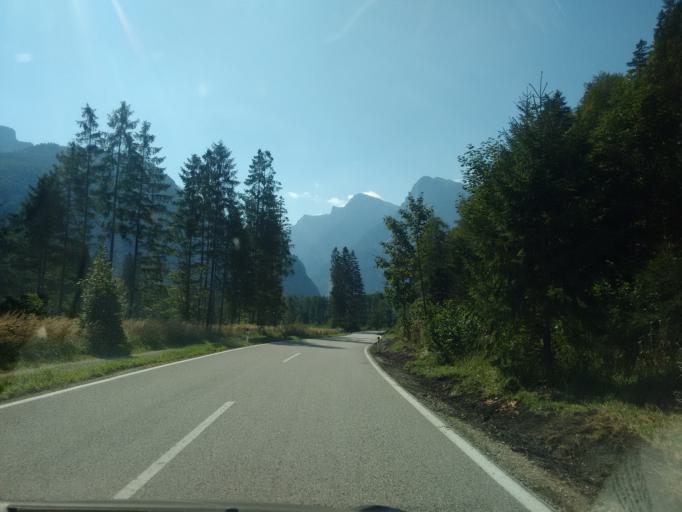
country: AT
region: Upper Austria
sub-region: Politischer Bezirk Gmunden
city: Gruenau im Almtal
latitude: 47.7597
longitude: 13.9537
